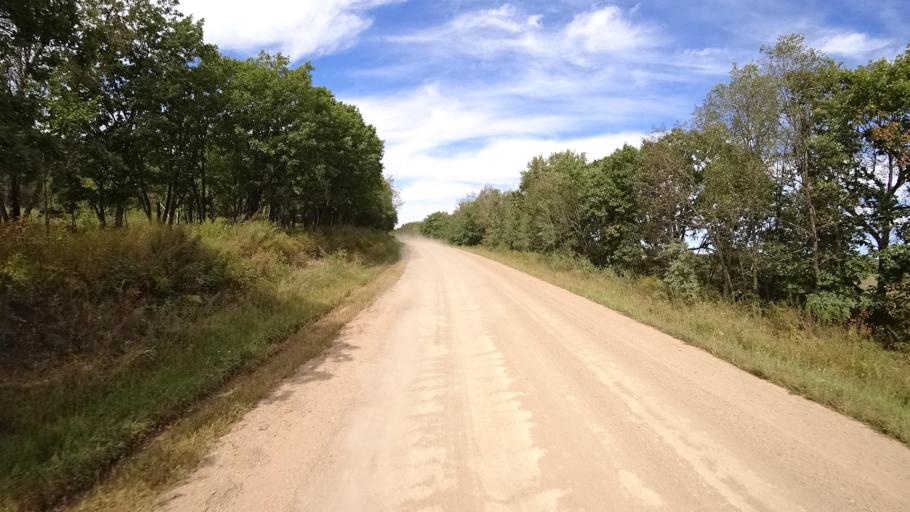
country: RU
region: Primorskiy
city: Yakovlevka
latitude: 44.5974
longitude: 133.6060
